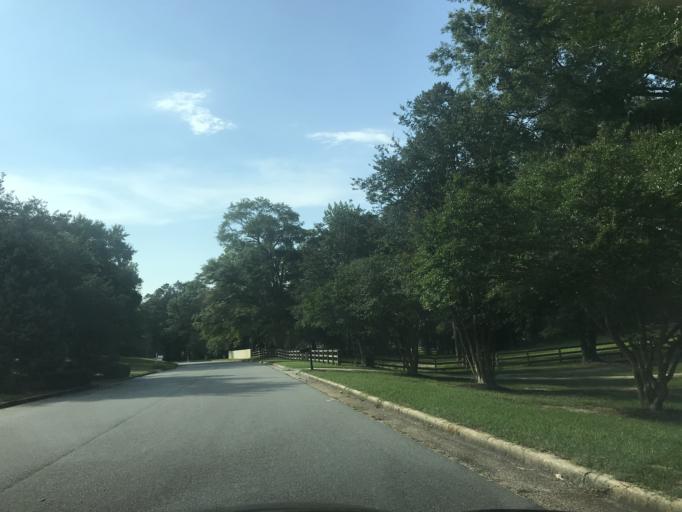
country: US
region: North Carolina
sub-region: Wake County
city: Knightdale
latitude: 35.8248
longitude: -78.5454
